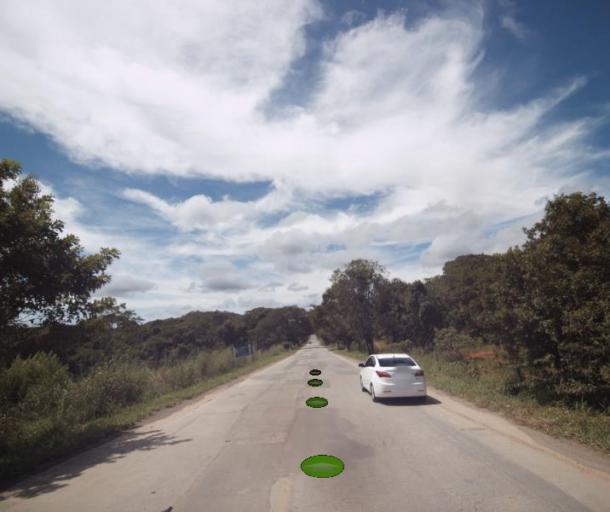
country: BR
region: Goias
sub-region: Padre Bernardo
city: Padre Bernardo
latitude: -15.5014
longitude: -48.2172
